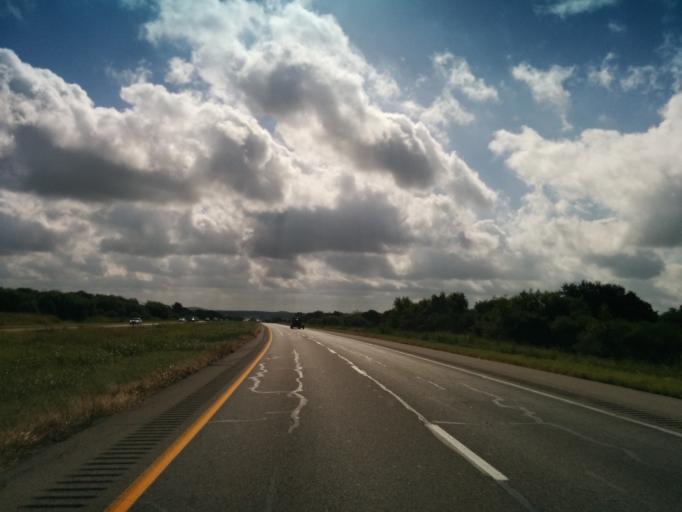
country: US
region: Texas
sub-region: Caldwell County
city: Luling
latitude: 29.6483
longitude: -97.6175
